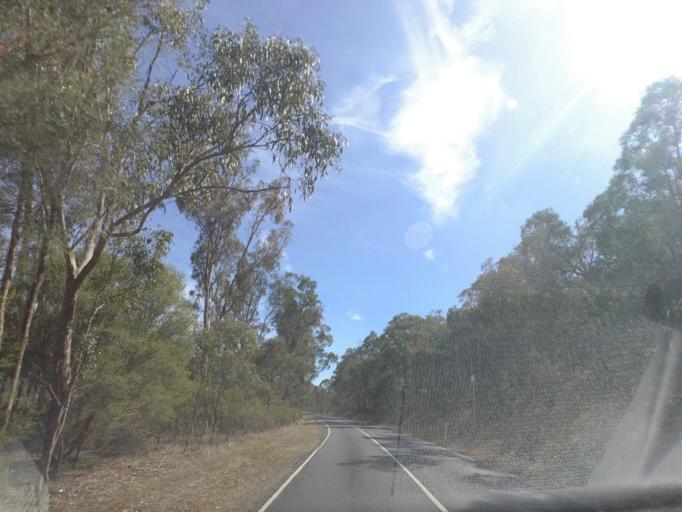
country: AU
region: Victoria
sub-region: Nillumbik
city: Saint Andrews
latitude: -37.6098
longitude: 145.2380
